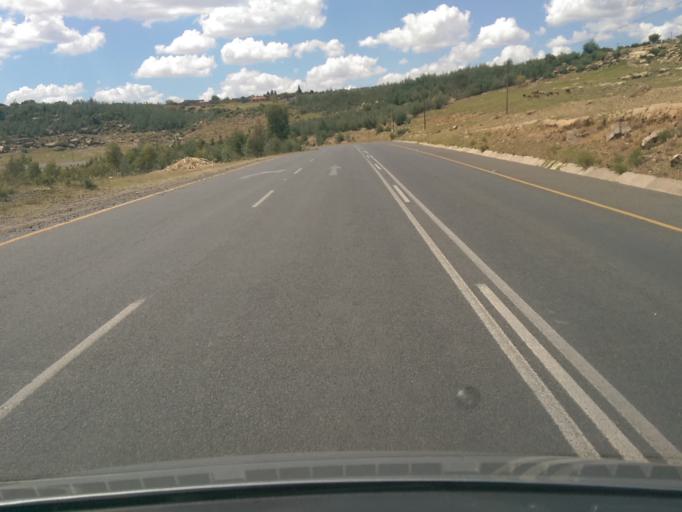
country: LS
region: Maseru
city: Maseru
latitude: -29.3977
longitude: 27.5288
